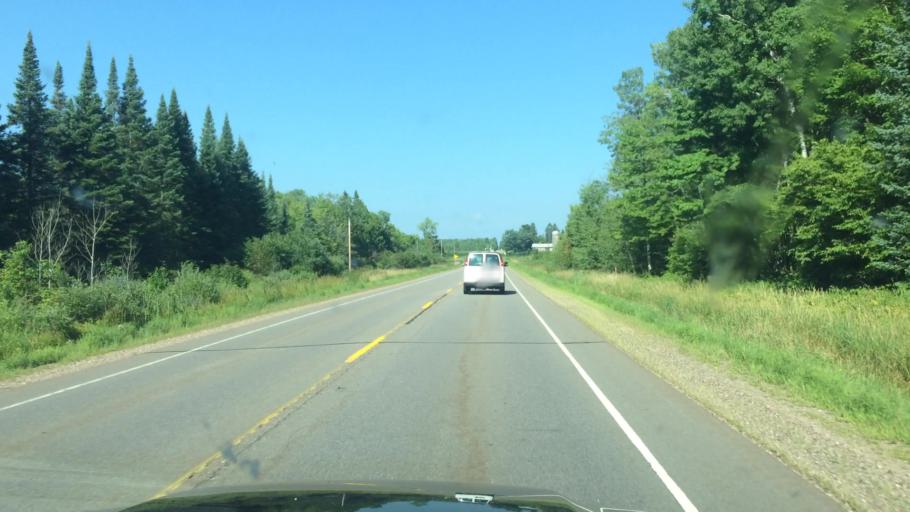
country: US
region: Wisconsin
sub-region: Lincoln County
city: Merrill
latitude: 45.1484
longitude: -89.4544
